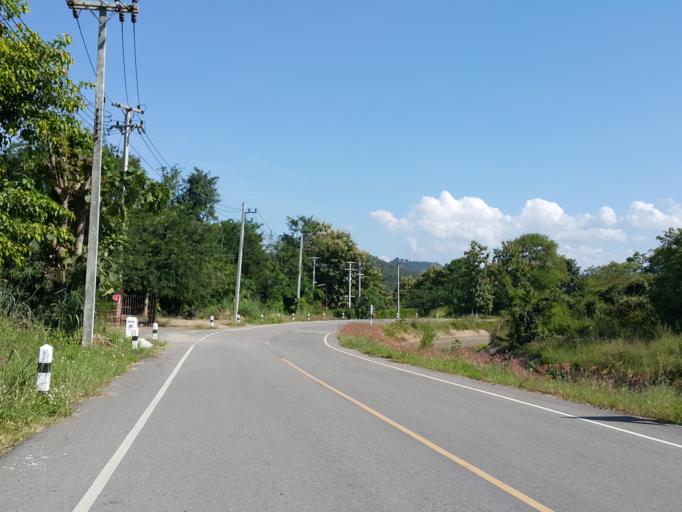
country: TH
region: Chiang Mai
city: Mae On
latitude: 18.8250
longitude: 99.1855
